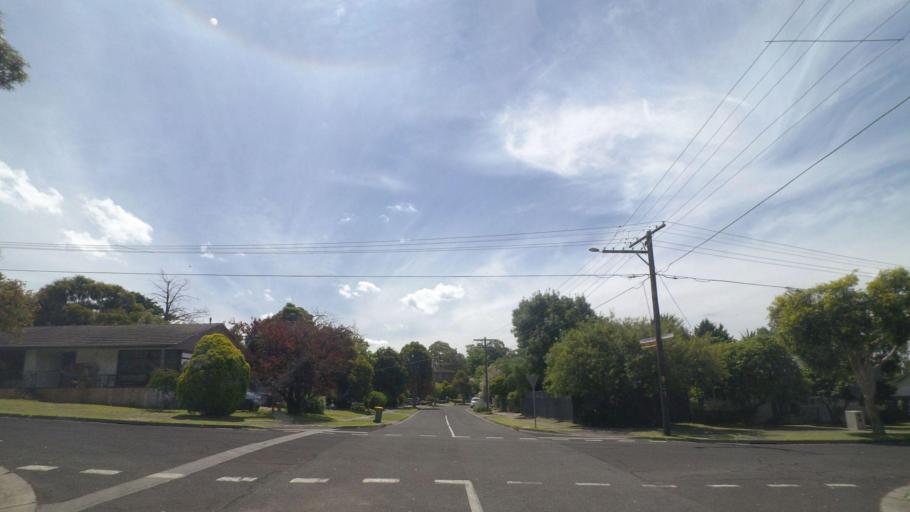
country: AU
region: Victoria
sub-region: Maroondah
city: Bayswater North
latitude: -37.8420
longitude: 145.2941
